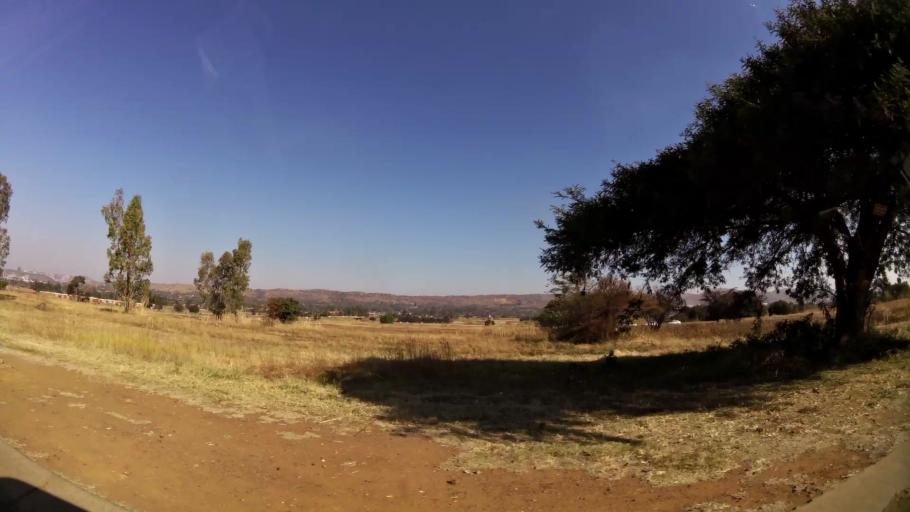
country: ZA
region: Gauteng
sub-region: City of Tshwane Metropolitan Municipality
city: Pretoria
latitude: -25.6966
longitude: 28.1376
